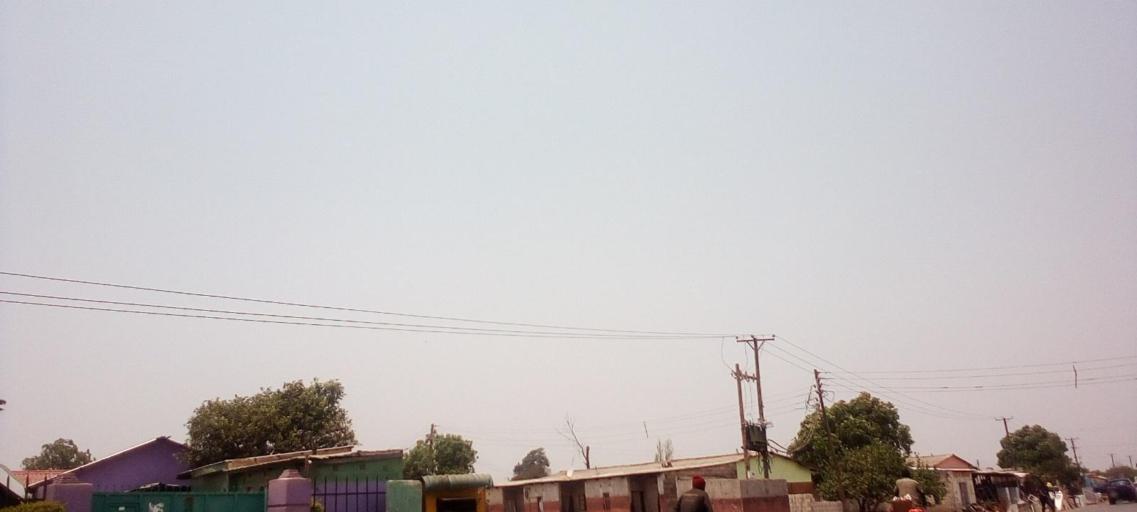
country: ZM
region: Lusaka
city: Lusaka
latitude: -15.4415
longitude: 28.2518
